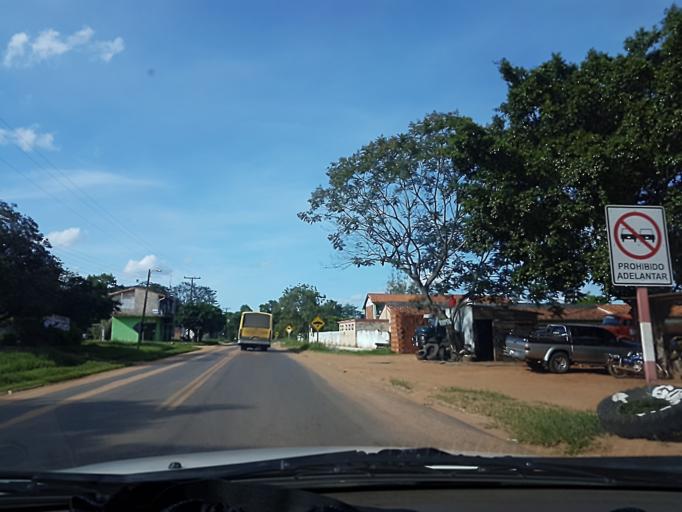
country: PY
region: Central
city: Limpio
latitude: -25.2200
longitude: -57.4475
